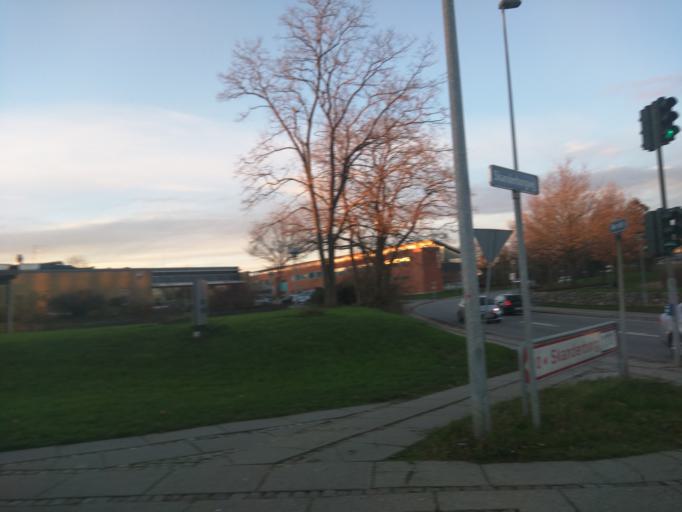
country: DK
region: Central Jutland
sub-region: Skanderborg Kommune
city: Horning
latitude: 56.0842
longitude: 10.0371
